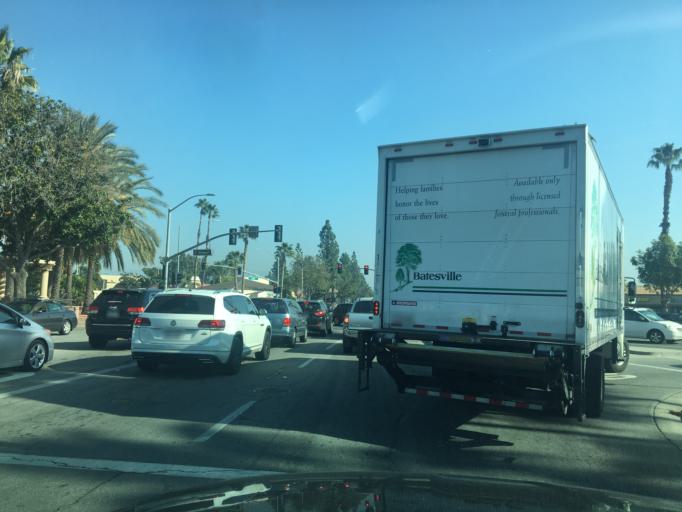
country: US
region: California
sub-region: Orange County
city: Tustin
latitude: 33.7421
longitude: -117.8188
